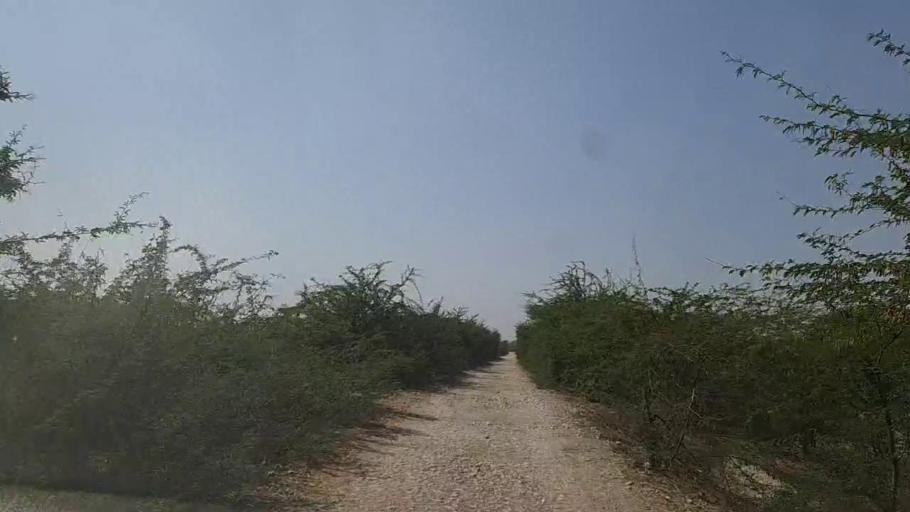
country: PK
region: Sindh
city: Naukot
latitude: 24.6514
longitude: 69.2807
